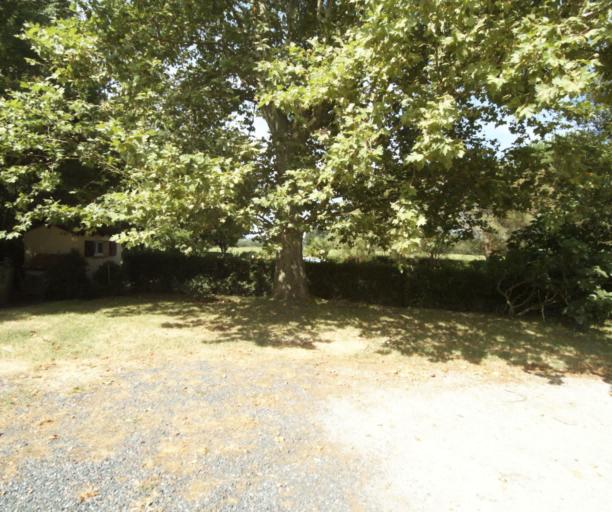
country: FR
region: Midi-Pyrenees
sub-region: Departement du Tarn
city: Soreze
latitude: 43.5079
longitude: 2.0498
